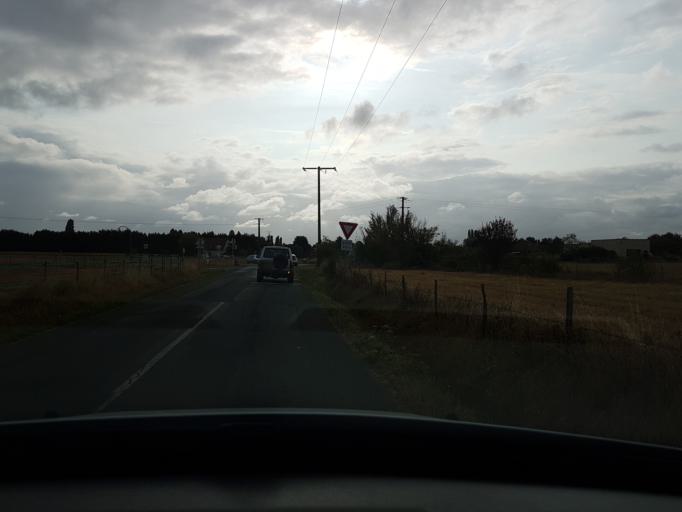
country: FR
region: Centre
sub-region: Departement d'Indre-et-Loire
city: Veretz
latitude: 47.3367
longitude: 0.8021
